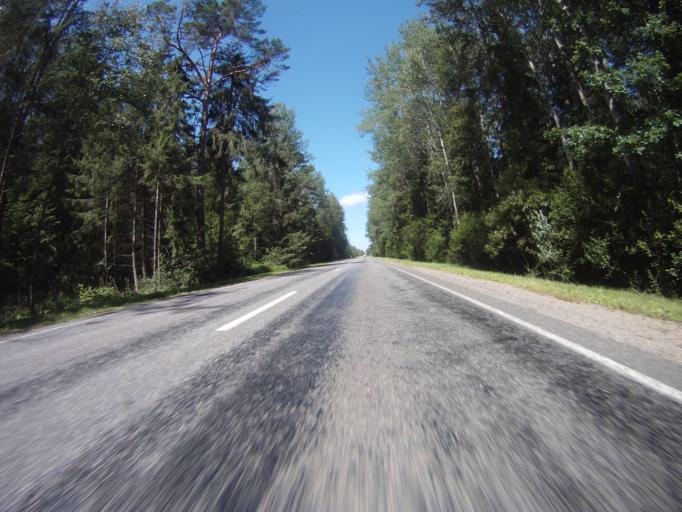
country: BY
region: Minsk
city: Il'ya
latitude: 54.3654
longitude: 27.4064
